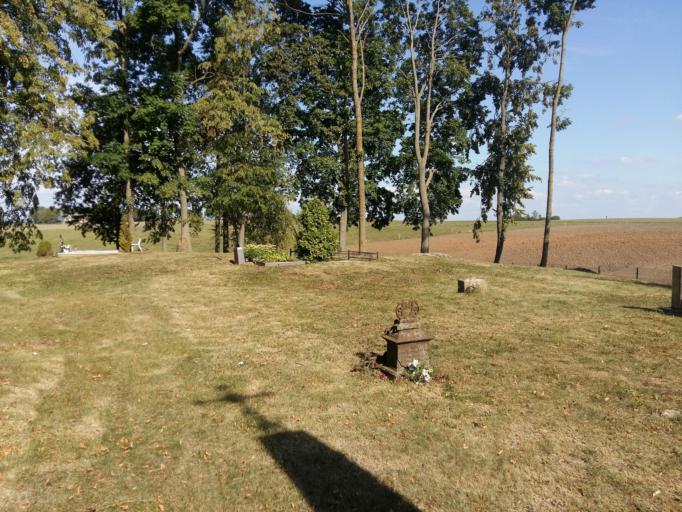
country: LT
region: Marijampoles apskritis
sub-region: Marijampole Municipality
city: Marijampole
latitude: 54.5229
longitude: 23.2639
